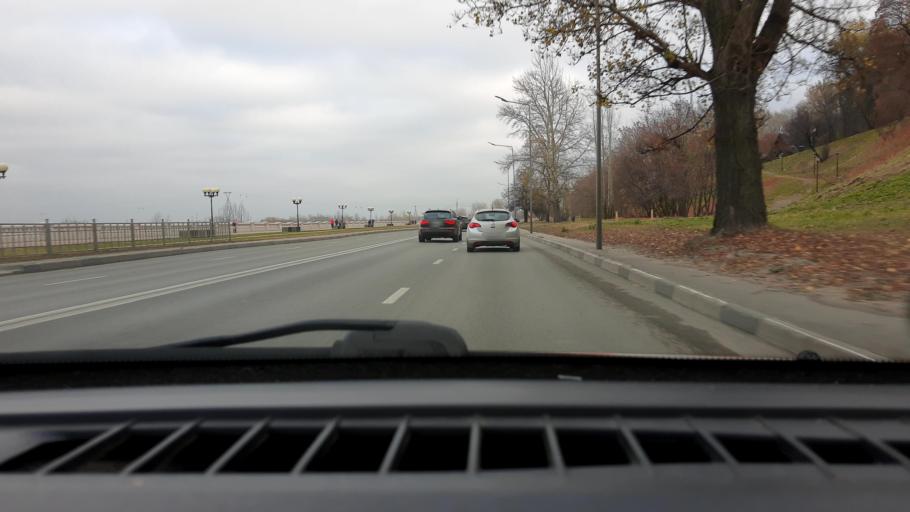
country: RU
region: Nizjnij Novgorod
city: Nizhniy Novgorod
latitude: 56.3330
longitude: 44.0218
